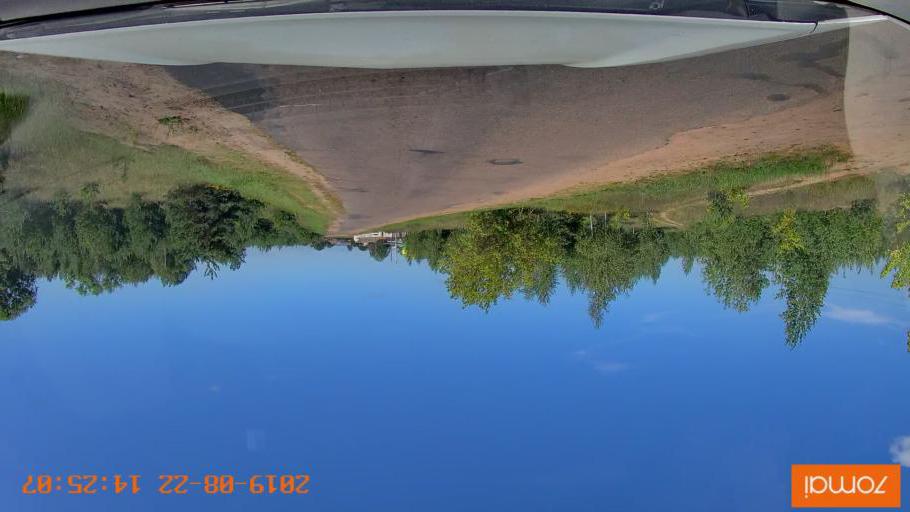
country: BY
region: Mogilev
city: Asipovichy
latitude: 53.3006
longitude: 28.6033
